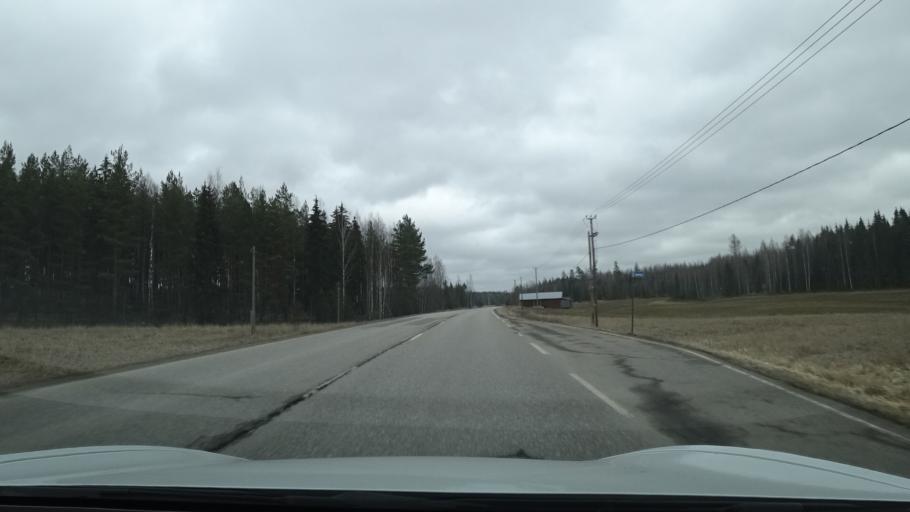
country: FI
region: Uusimaa
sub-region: Porvoo
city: Pukkila
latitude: 60.6436
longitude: 25.6360
